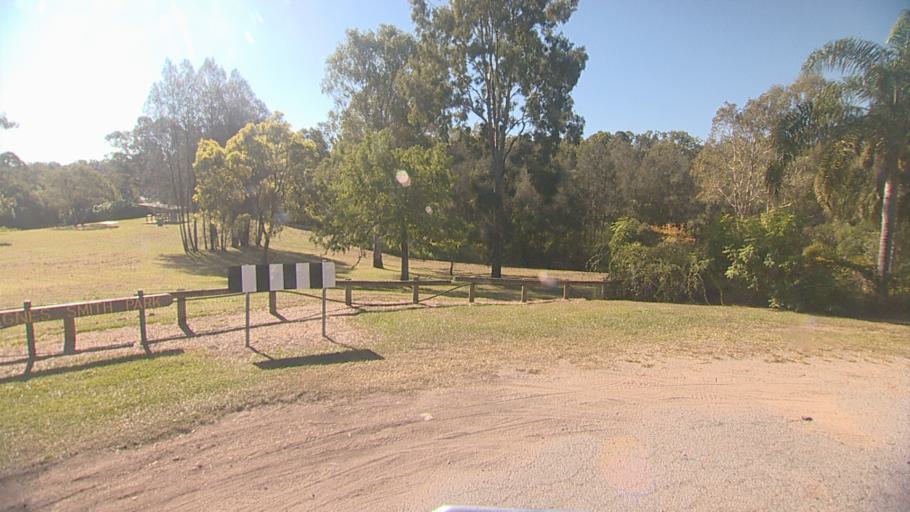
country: AU
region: Queensland
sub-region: Logan
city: Logan Reserve
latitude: -27.7422
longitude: 153.1221
